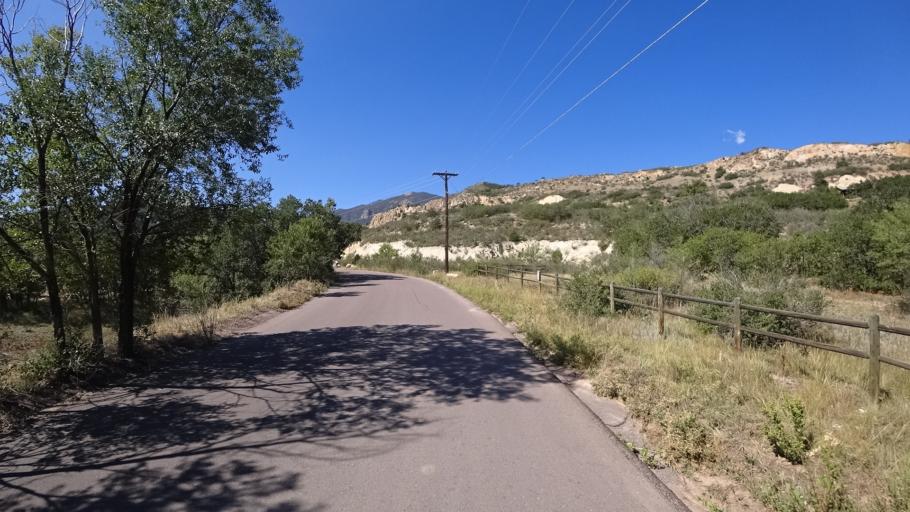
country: US
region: Colorado
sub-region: El Paso County
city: Manitou Springs
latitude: 38.8306
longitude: -104.8810
